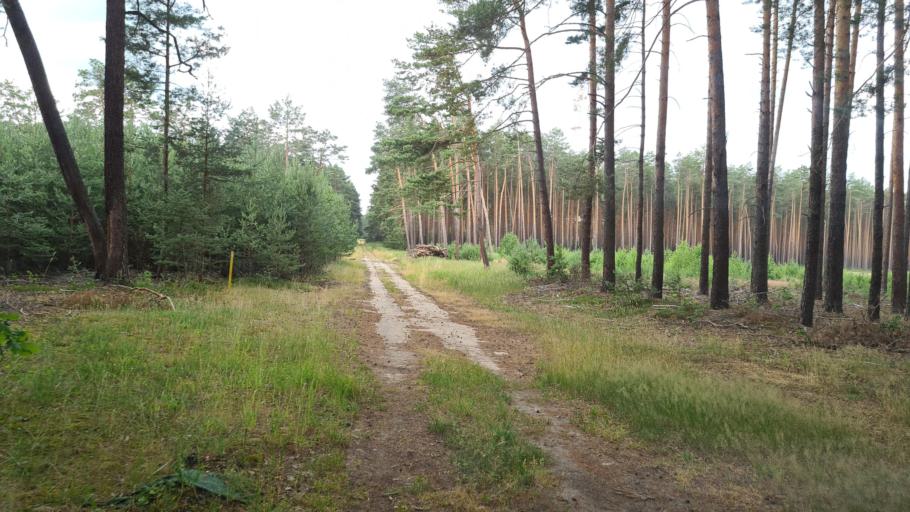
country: DE
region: Brandenburg
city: Crinitz
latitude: 51.7266
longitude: 13.7146
